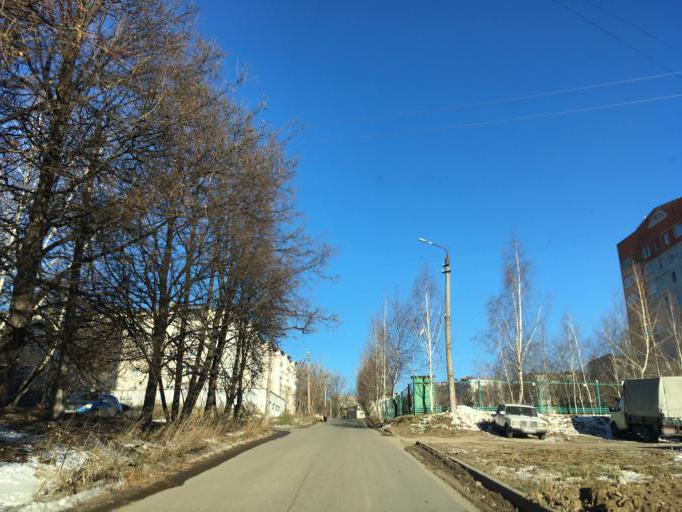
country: RU
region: Tula
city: Tula
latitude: 54.1921
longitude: 37.6758
